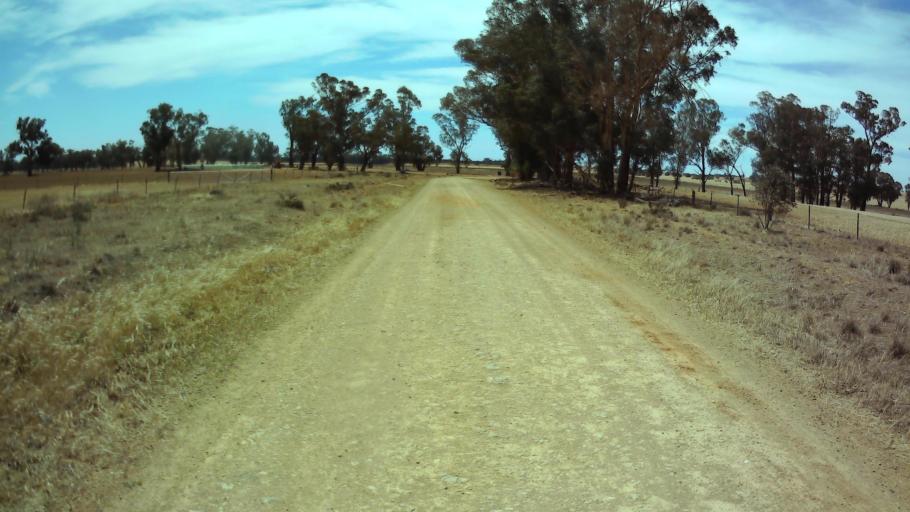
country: AU
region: New South Wales
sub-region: Weddin
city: Grenfell
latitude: -33.7596
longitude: 148.1402
